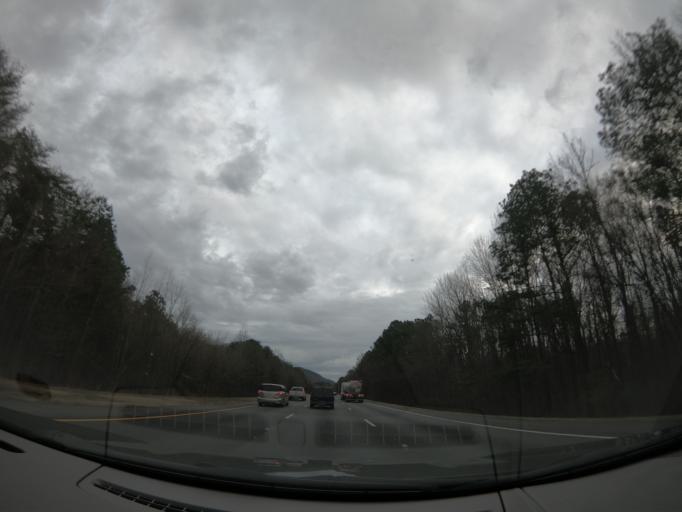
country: US
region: Georgia
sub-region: Whitfield County
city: Dalton
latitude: 34.8182
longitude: -85.0179
